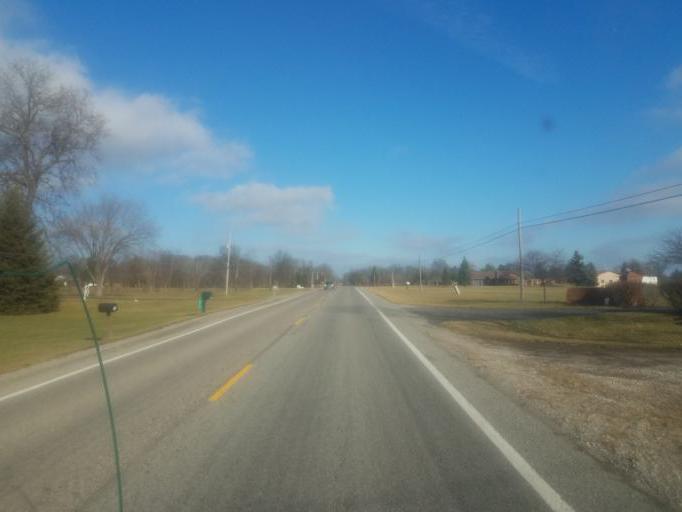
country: US
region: Ohio
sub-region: Crawford County
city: Galion
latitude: 40.7043
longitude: -82.8158
